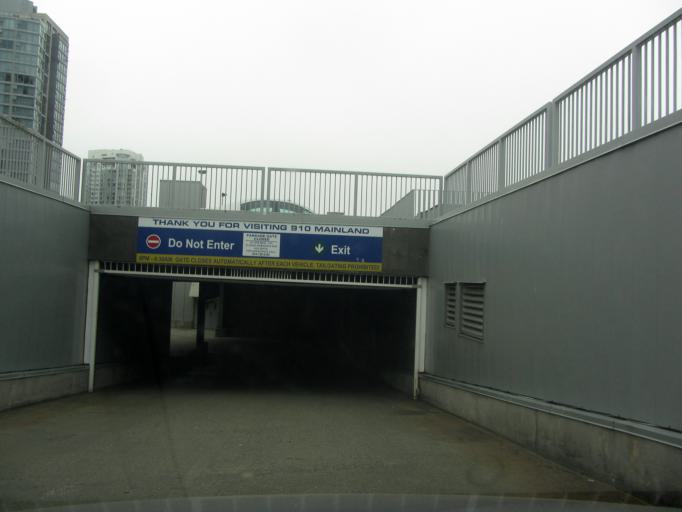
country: CA
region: British Columbia
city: West End
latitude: 49.2780
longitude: -123.1168
